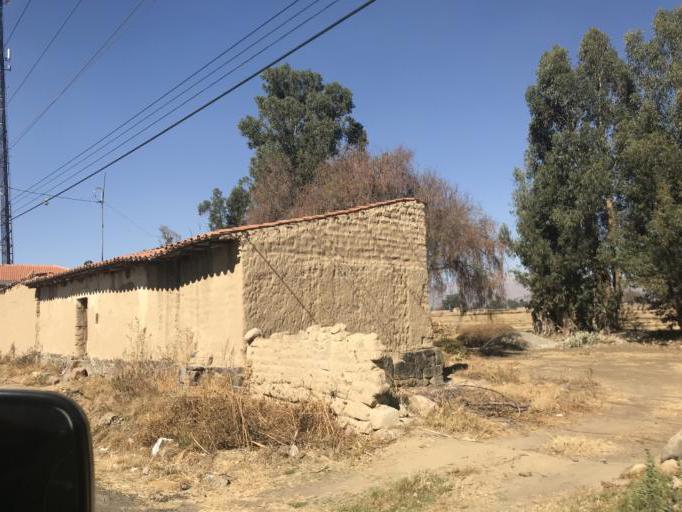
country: BO
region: Cochabamba
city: Punata
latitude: -17.5593
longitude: -65.8692
